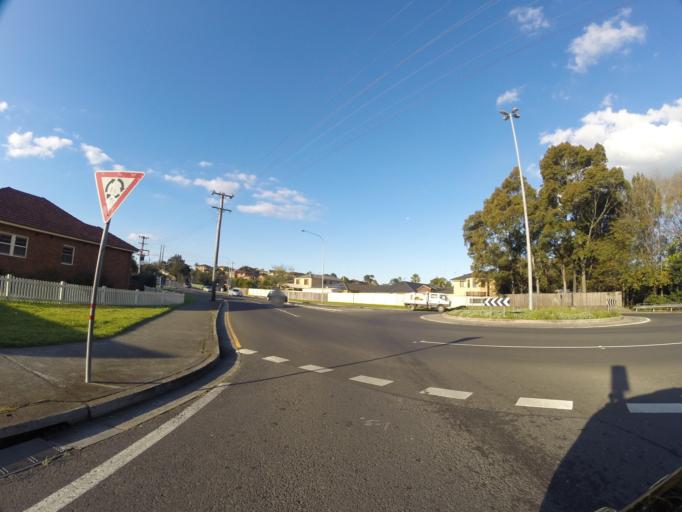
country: AU
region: New South Wales
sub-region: Wollongong
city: Cordeaux Heights
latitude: -34.4472
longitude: 150.8515
